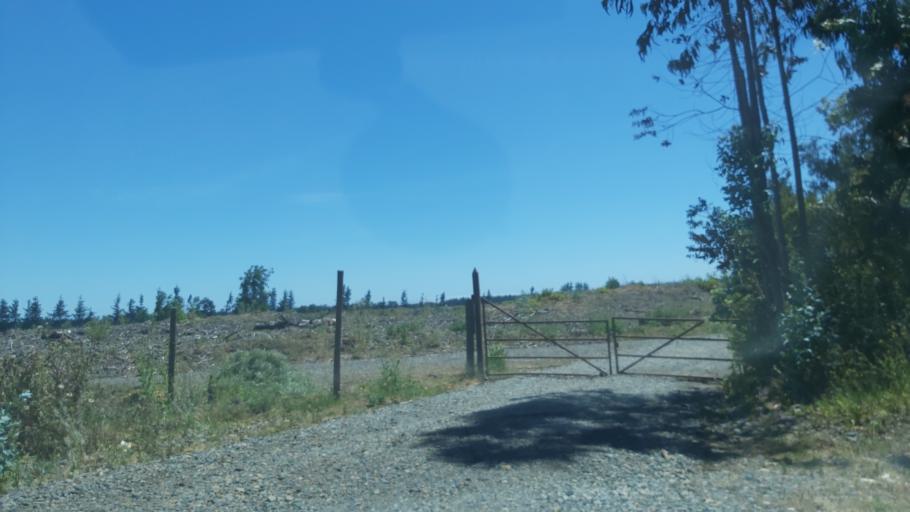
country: CL
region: Maule
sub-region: Provincia de Talca
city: Constitucion
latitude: -35.1540
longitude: -72.2238
